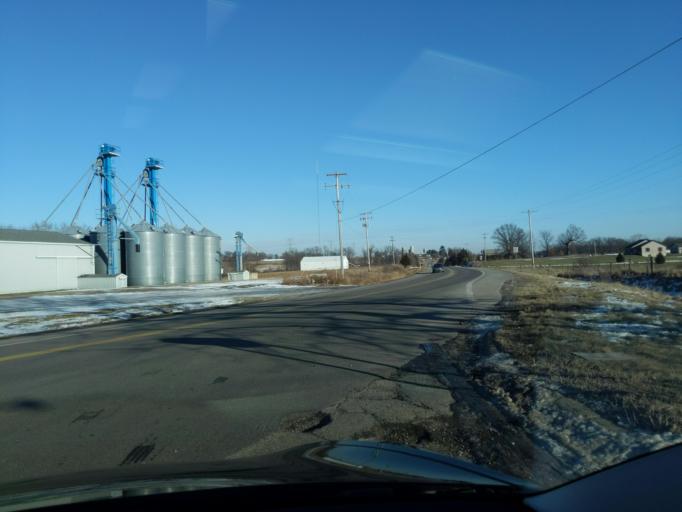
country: US
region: Michigan
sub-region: Ingham County
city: Stockbridge
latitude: 42.4190
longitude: -84.1673
